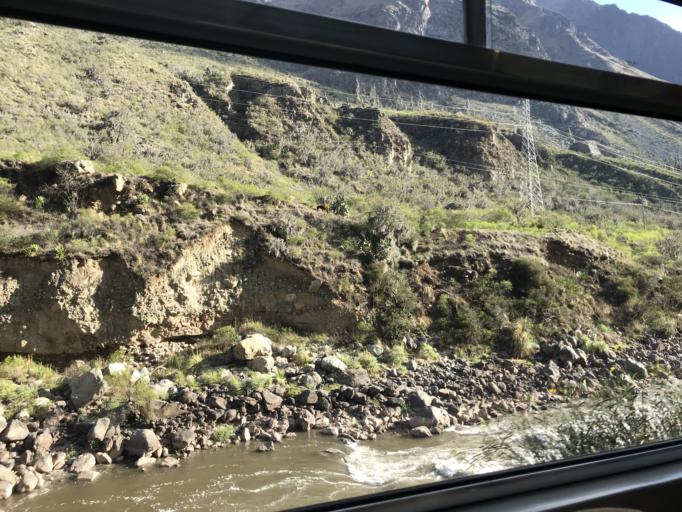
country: PE
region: Cusco
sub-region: Provincia de Urubamba
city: Ollantaytambo
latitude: -13.2244
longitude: -72.3971
